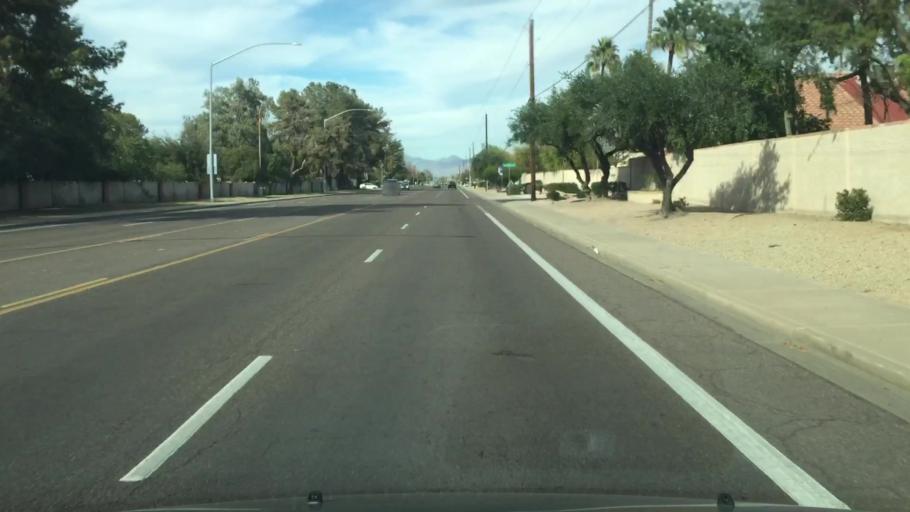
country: US
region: Arizona
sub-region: Maricopa County
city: Mesa
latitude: 33.4392
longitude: -111.8052
